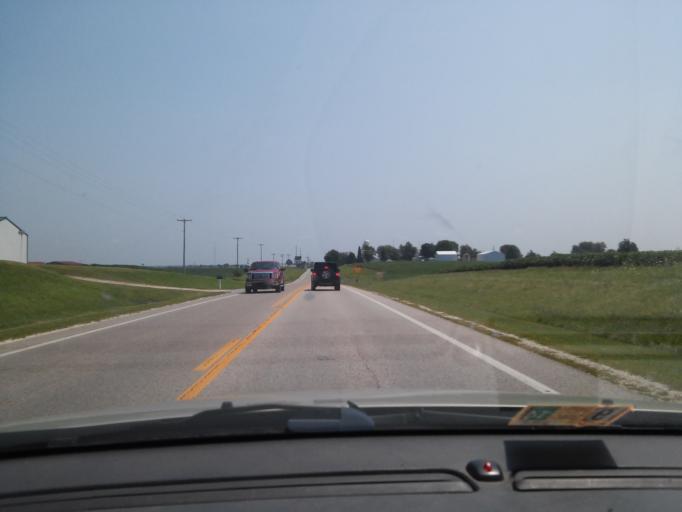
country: US
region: Illinois
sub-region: Pike County
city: Pittsfield
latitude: 39.6048
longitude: -90.8526
